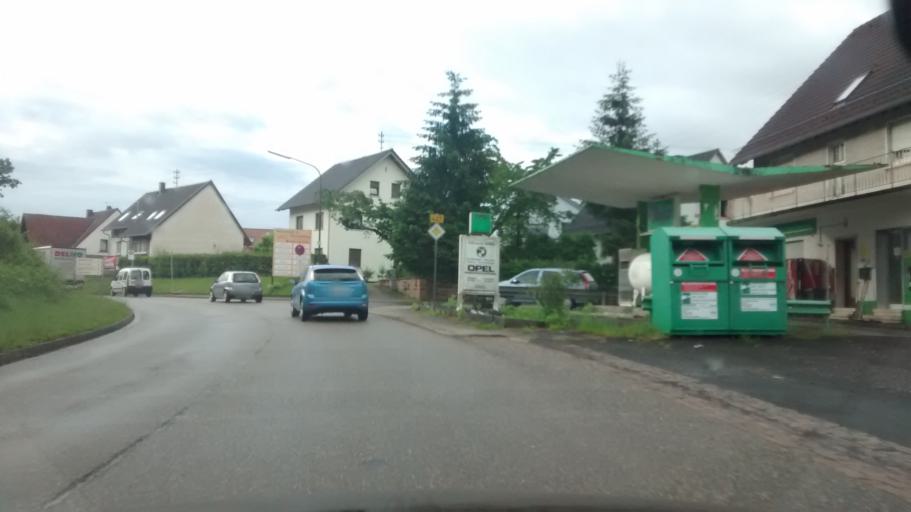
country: DE
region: Rheinland-Pfalz
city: Busenberg
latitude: 49.1321
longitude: 7.8229
